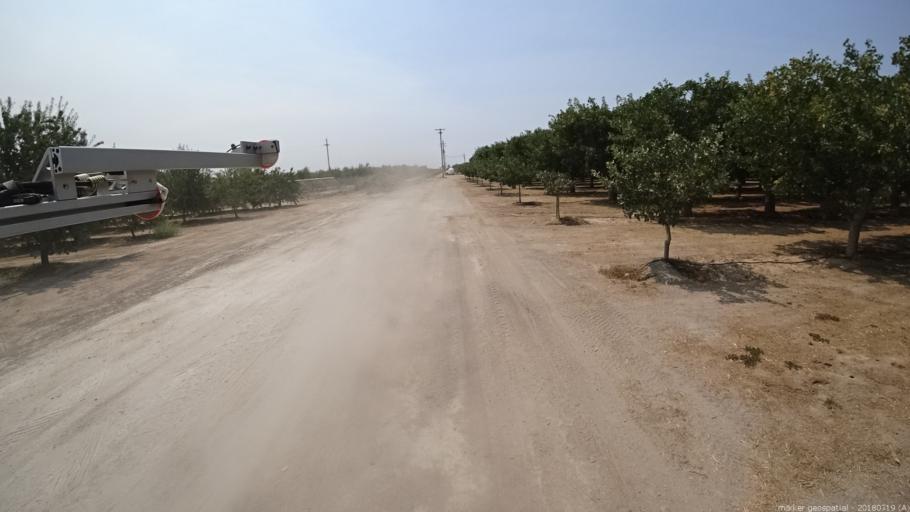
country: US
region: California
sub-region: Madera County
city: Fairmead
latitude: 37.1027
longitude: -120.1840
